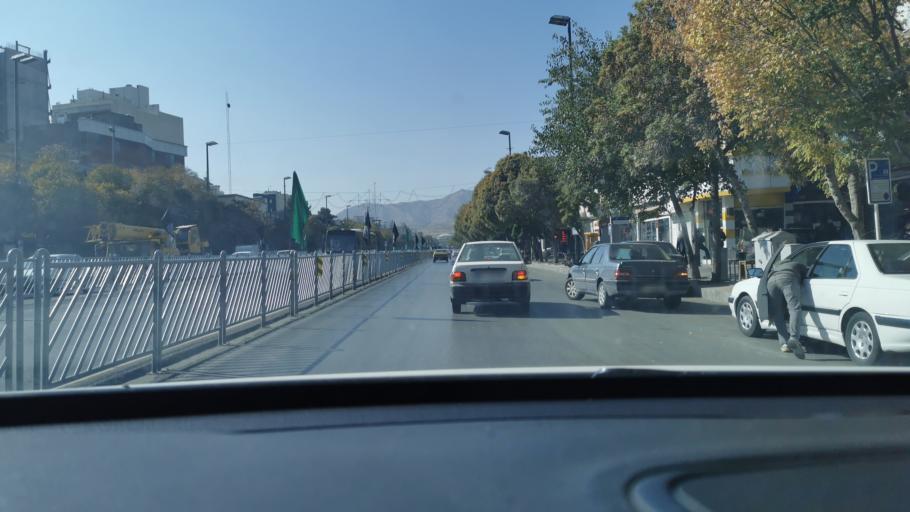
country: IR
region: Razavi Khorasan
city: Mashhad
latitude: 36.2721
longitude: 59.6020
